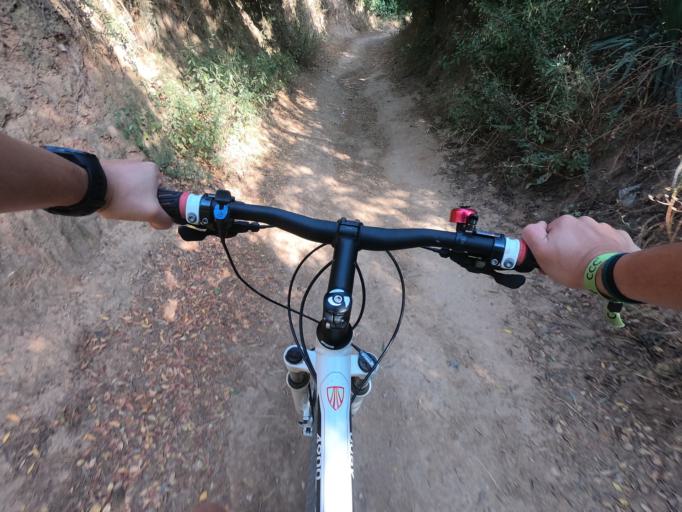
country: ES
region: Catalonia
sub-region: Provincia de Barcelona
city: Sant Just Desvern
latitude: 41.3861
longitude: 2.0654
